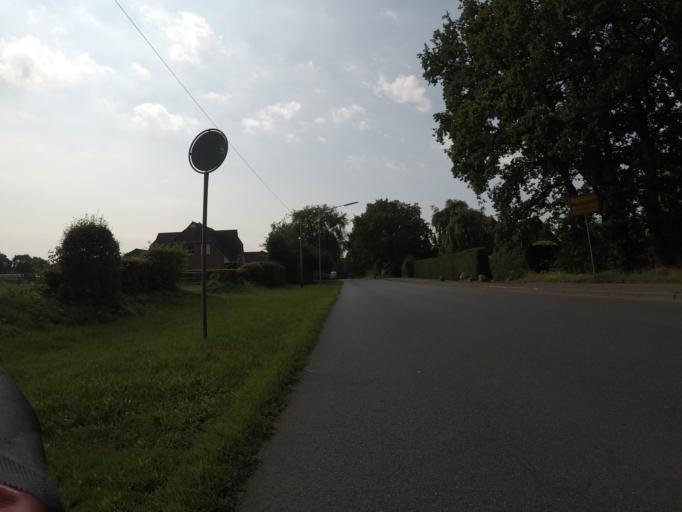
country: DE
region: Schleswig-Holstein
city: Tangstedt
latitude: 53.7102
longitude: 10.0580
